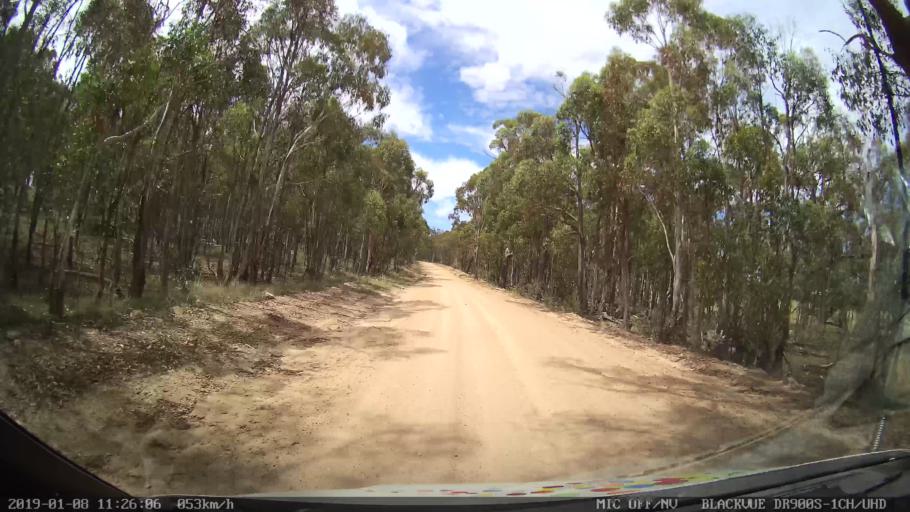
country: AU
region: New South Wales
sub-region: Guyra
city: Guyra
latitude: -30.2777
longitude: 151.5585
